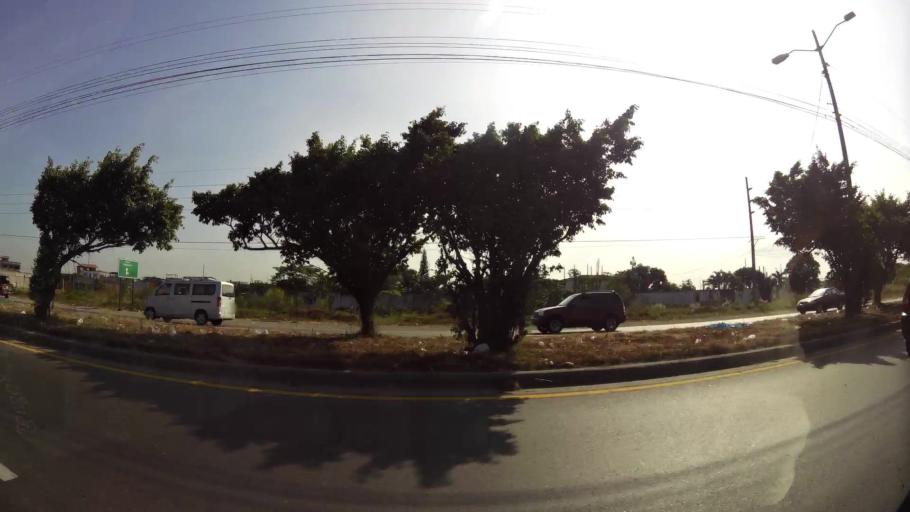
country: EC
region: Guayas
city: Eloy Alfaro
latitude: -2.1838
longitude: -79.8147
